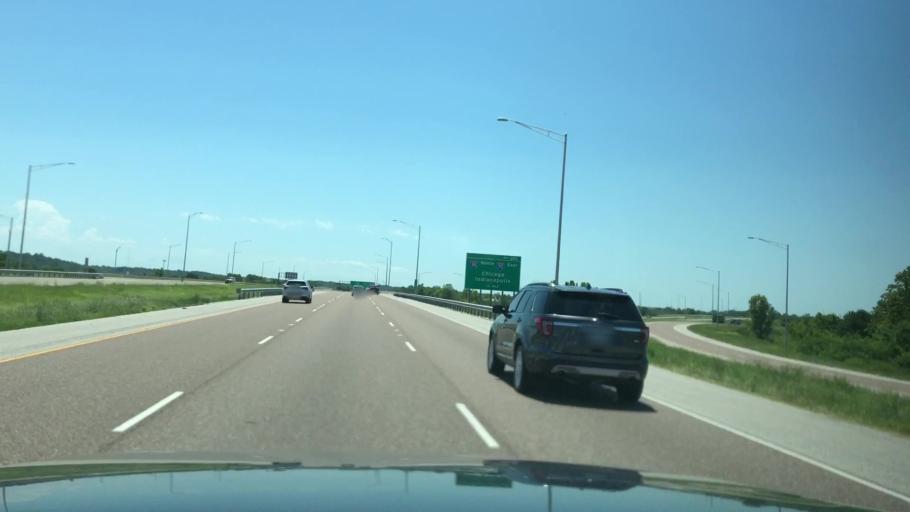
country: US
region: Illinois
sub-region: Saint Clair County
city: Caseyville
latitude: 38.6782
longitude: -90.0300
